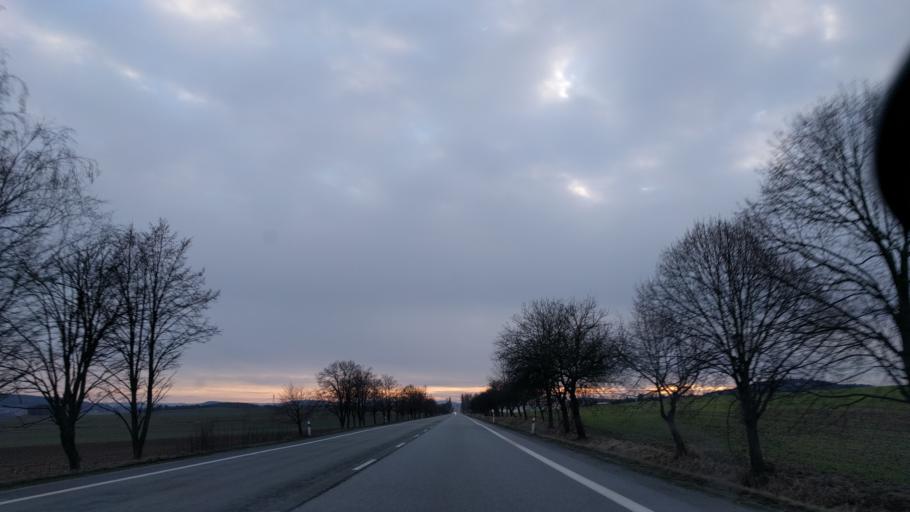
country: CZ
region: Jihocesky
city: Radomysl
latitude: 49.2882
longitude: 13.9685
